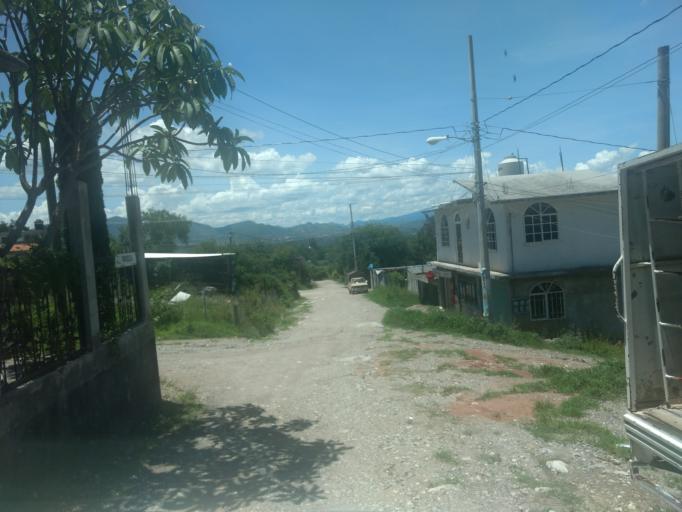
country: MX
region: Oaxaca
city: Ciudad de Huajuapam de Leon
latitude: 17.8183
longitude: -97.7940
